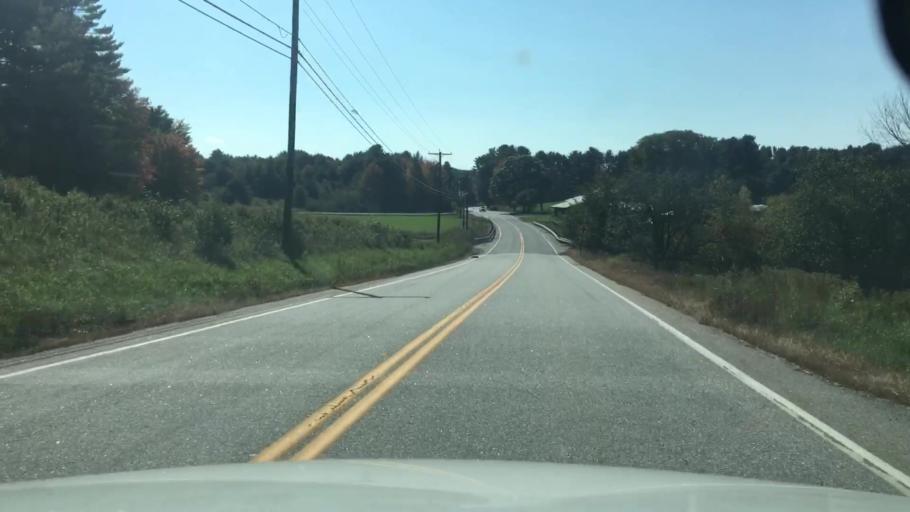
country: US
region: Maine
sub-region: Androscoggin County
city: Lisbon Falls
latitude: 44.0248
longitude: -70.0402
